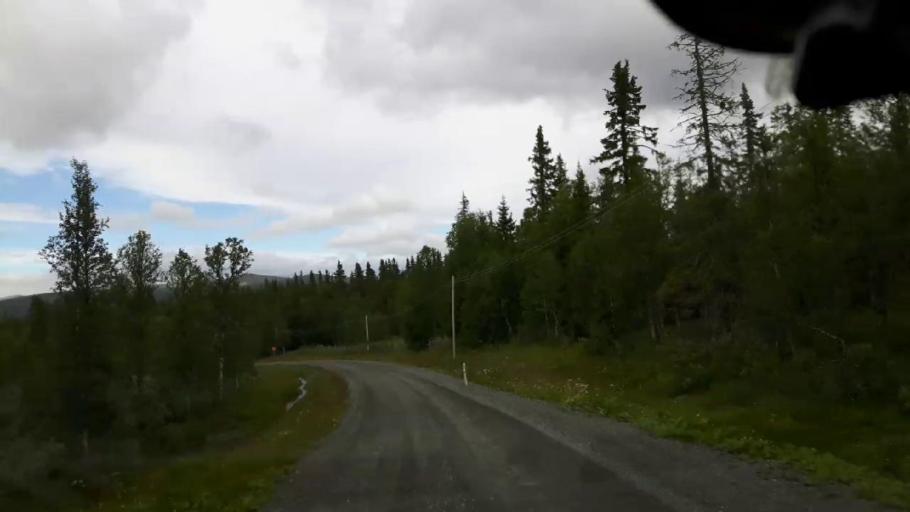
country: SE
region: Jaemtland
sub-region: Krokoms Kommun
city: Valla
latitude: 63.7784
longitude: 13.8296
